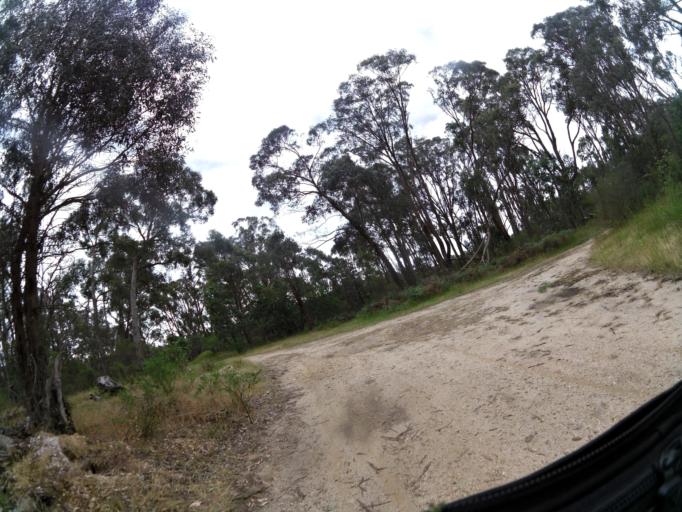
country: AU
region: Victoria
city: Brown Hill
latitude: -37.4384
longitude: 143.9062
